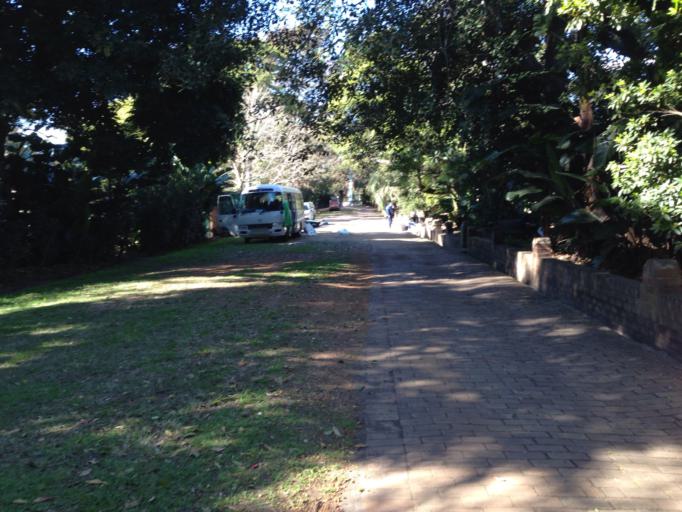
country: AU
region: New South Wales
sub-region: North Sydney
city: Wollstonecraft
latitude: -33.8239
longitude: 151.1894
